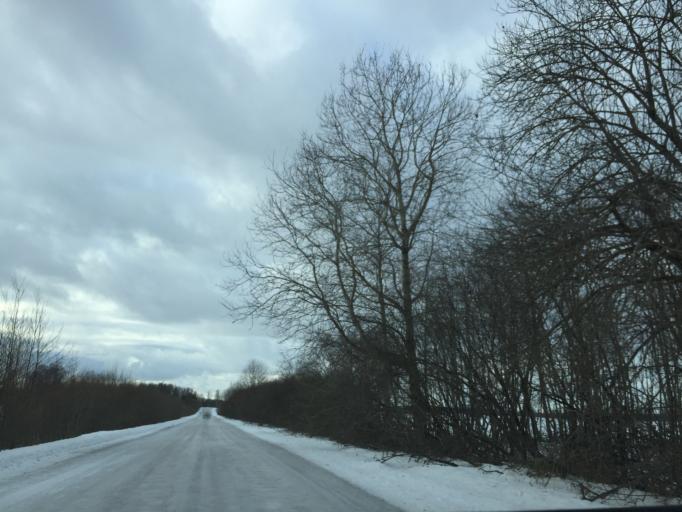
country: LV
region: Lielvarde
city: Lielvarde
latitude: 56.6038
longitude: 24.7493
